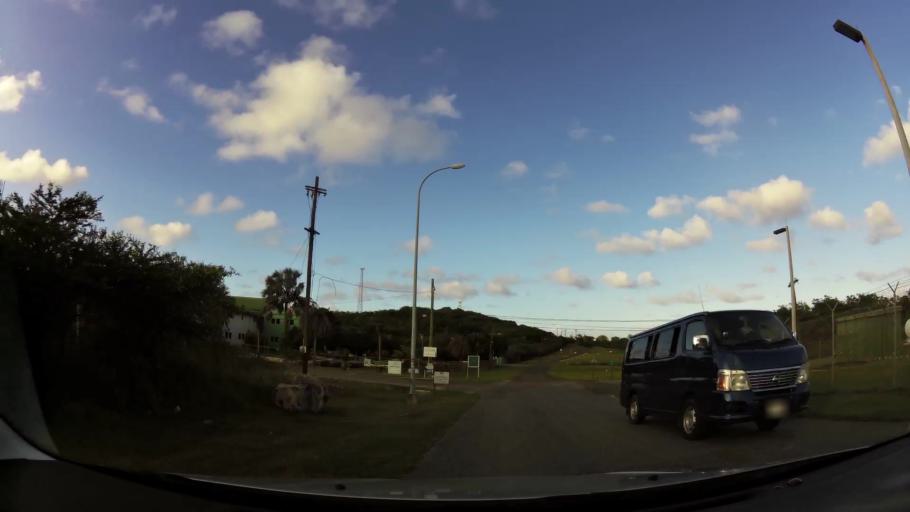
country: AG
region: Saint George
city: Piggotts
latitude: 17.1513
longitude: -61.7944
